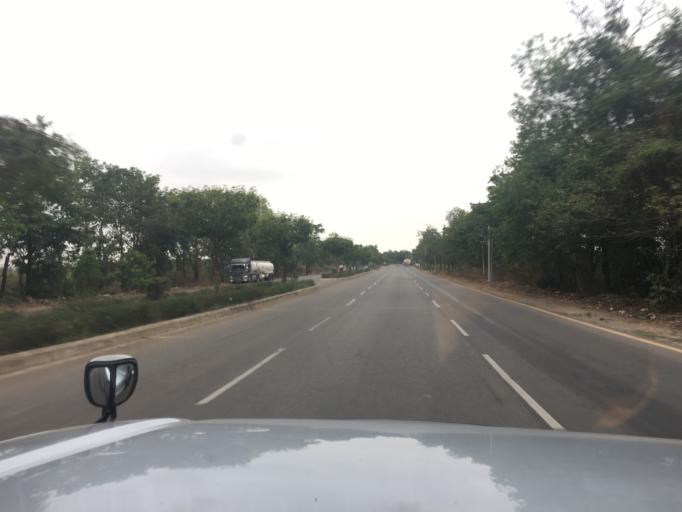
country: MM
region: Bago
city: Bago
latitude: 17.2293
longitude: 96.4564
